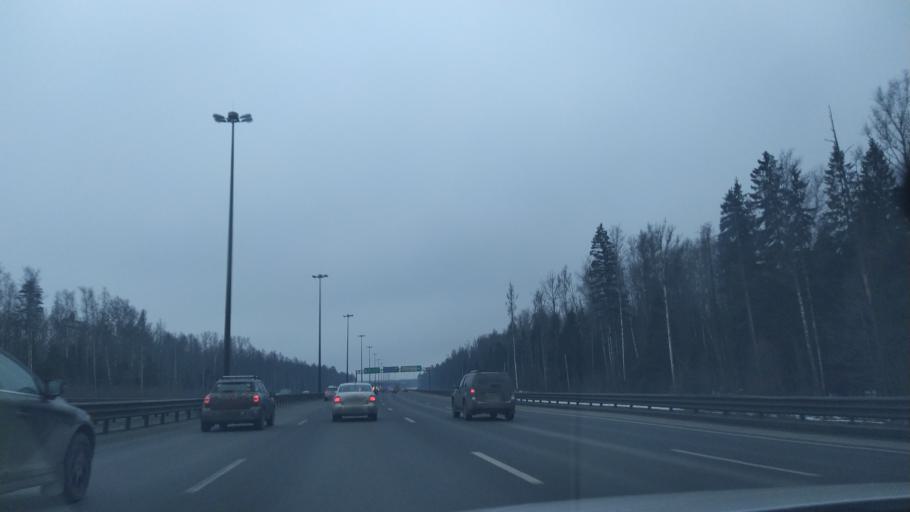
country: RU
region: Leningrad
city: Yanino Vtoroye
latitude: 59.9577
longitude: 30.5518
